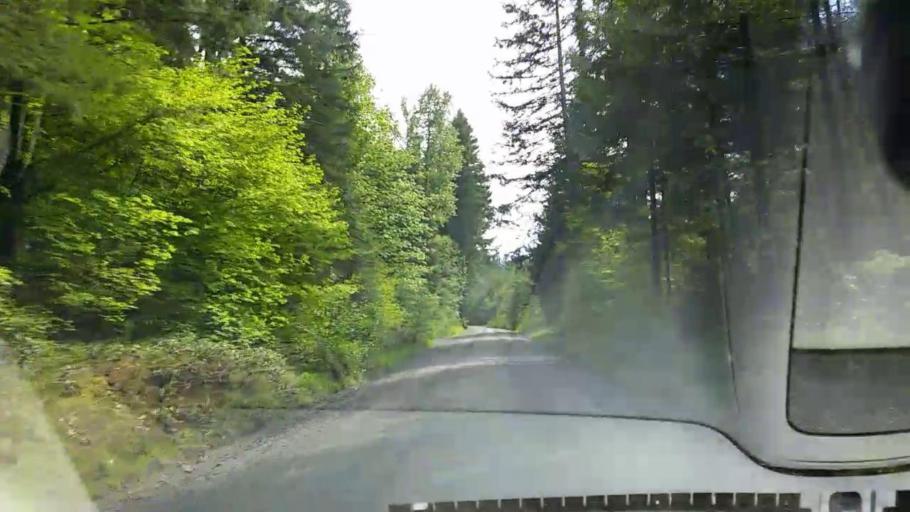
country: US
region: Washington
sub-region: Mason County
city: Shelton
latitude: 47.3599
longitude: -123.2843
